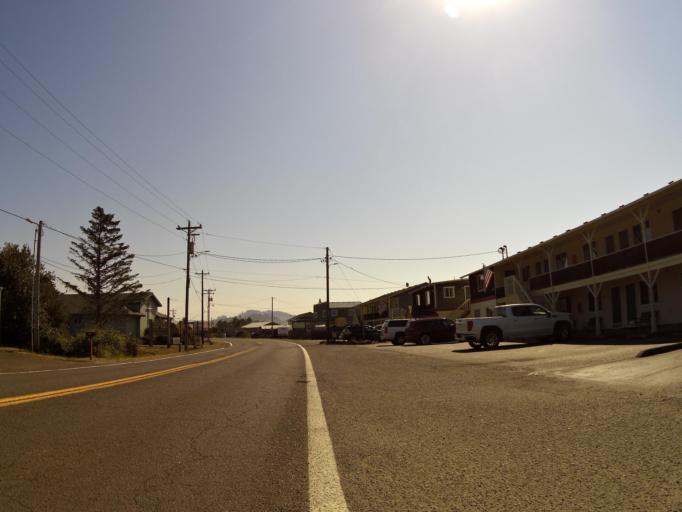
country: US
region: Oregon
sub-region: Tillamook County
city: Pacific City
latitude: 45.2003
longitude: -123.9612
